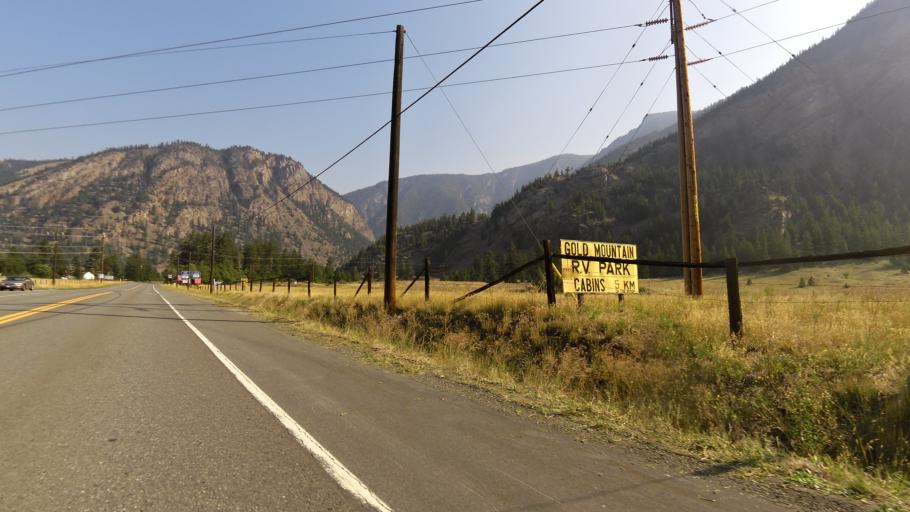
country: CA
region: British Columbia
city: Princeton
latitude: 49.3492
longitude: -120.0757
